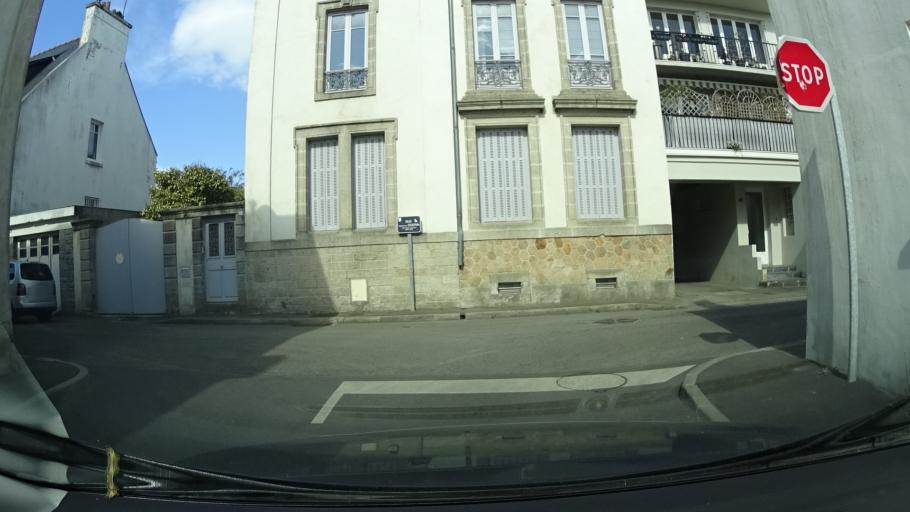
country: FR
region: Brittany
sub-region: Departement du Morbihan
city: Vannes
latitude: 47.6546
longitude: -2.7659
